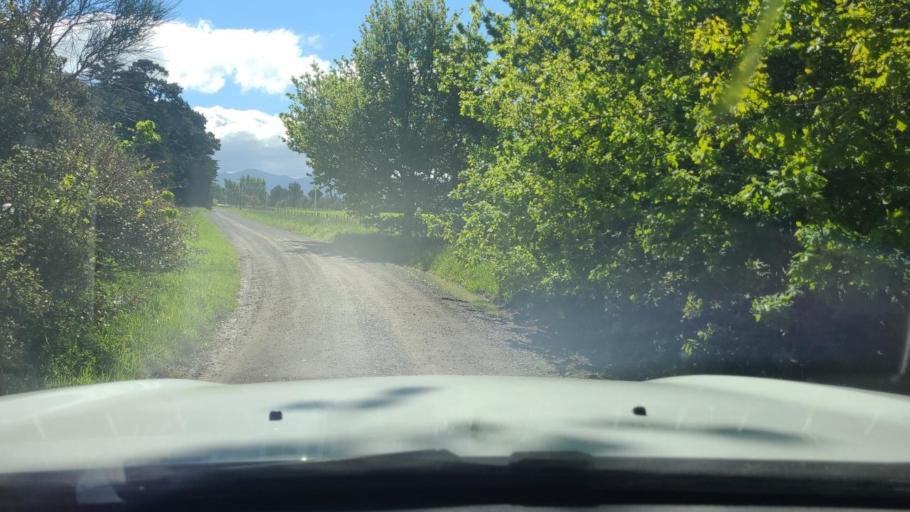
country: NZ
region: Wellington
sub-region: South Wairarapa District
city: Waipawa
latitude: -41.2308
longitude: 175.3234
